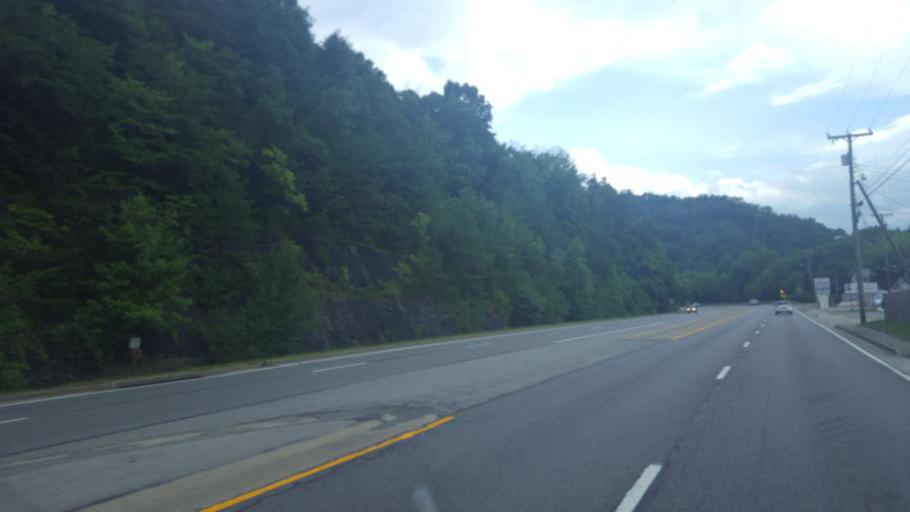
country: US
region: Kentucky
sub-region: Pike County
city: Pikeville
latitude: 37.4491
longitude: -82.5249
